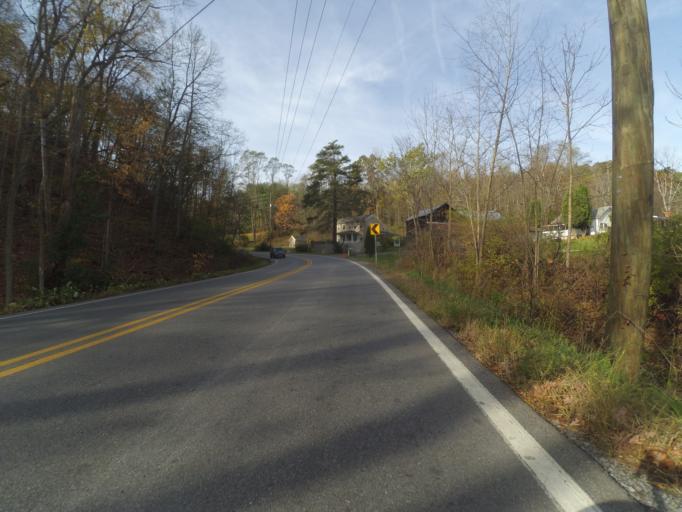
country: US
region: Pennsylvania
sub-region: Centre County
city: Park Forest Village
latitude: 40.8285
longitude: -77.9654
